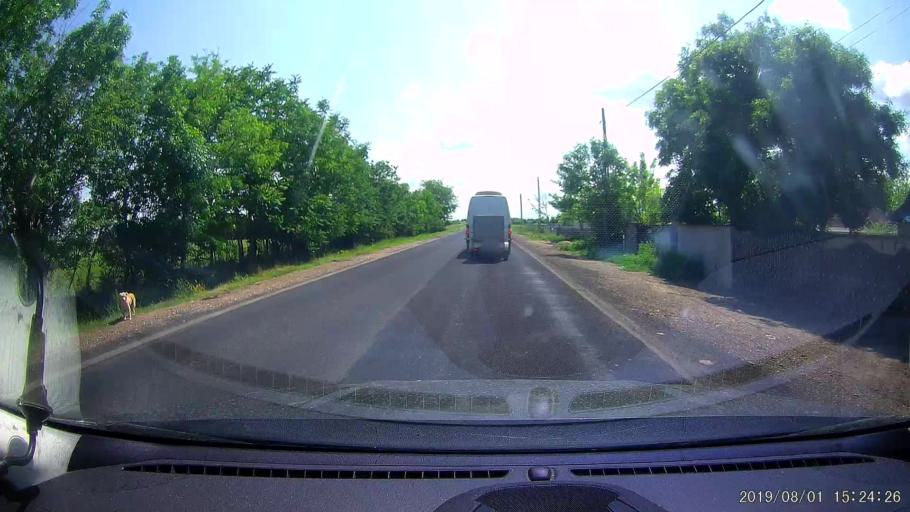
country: RO
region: Braila
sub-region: Comuna Viziru
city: Lanurile
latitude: 45.0330
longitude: 27.7494
